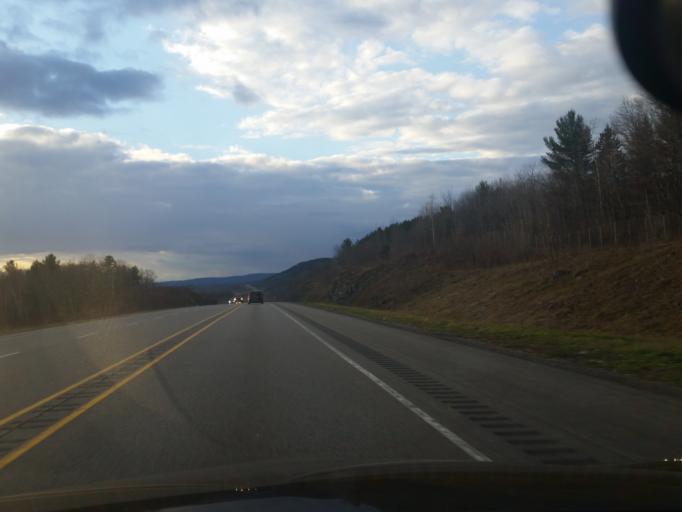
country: CA
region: Ontario
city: Hawkesbury
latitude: 45.6511
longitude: -74.7619
